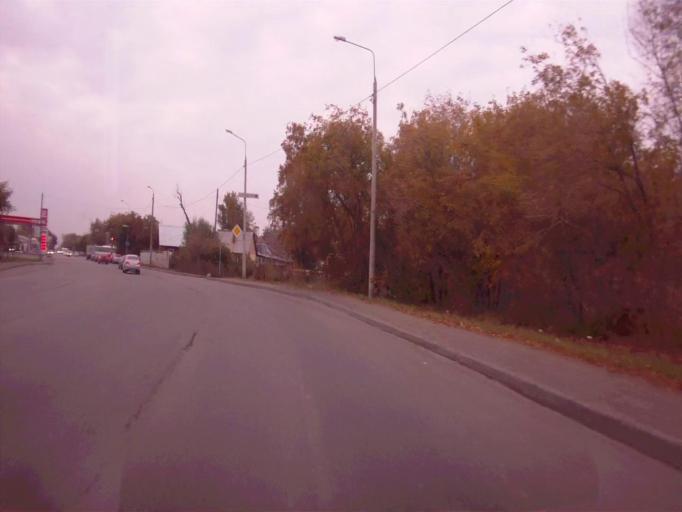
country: RU
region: Chelyabinsk
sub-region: Gorod Chelyabinsk
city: Chelyabinsk
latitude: 55.1330
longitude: 61.3851
